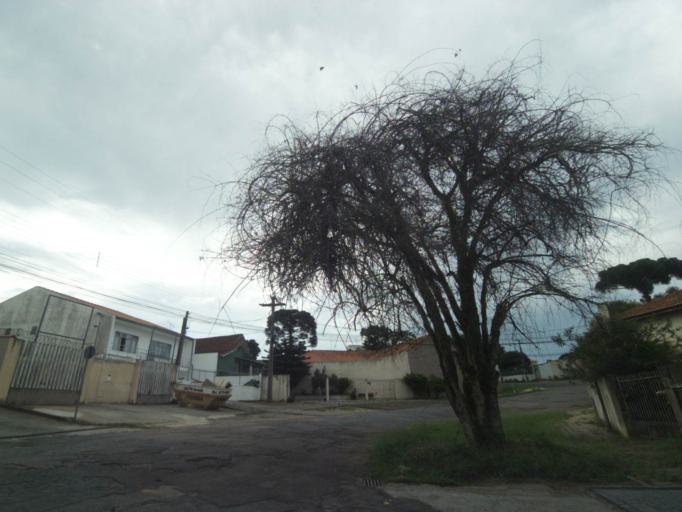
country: BR
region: Parana
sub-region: Pinhais
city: Pinhais
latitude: -25.4449
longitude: -49.2301
